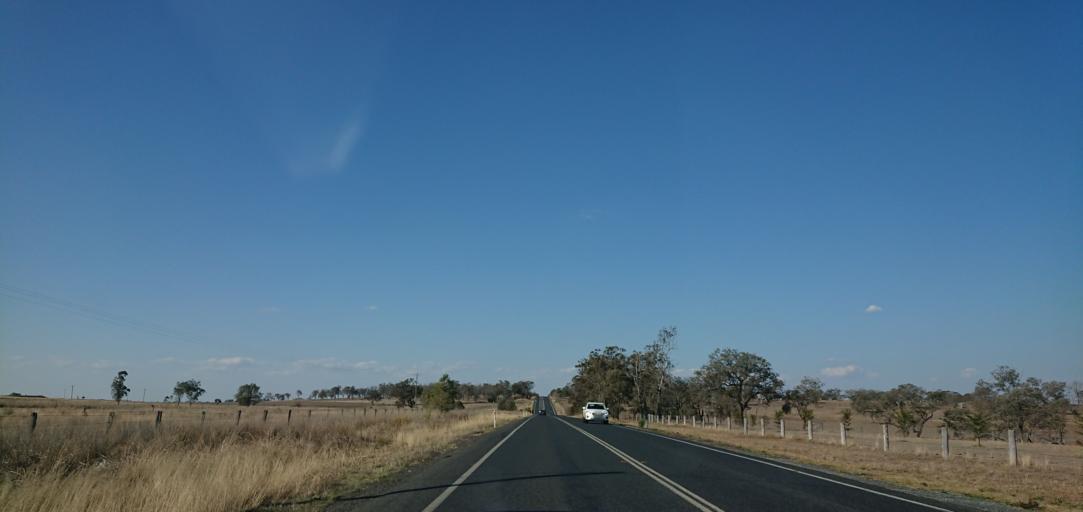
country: AU
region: Queensland
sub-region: Toowoomba
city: Westbrook
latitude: -27.6312
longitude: 151.7513
